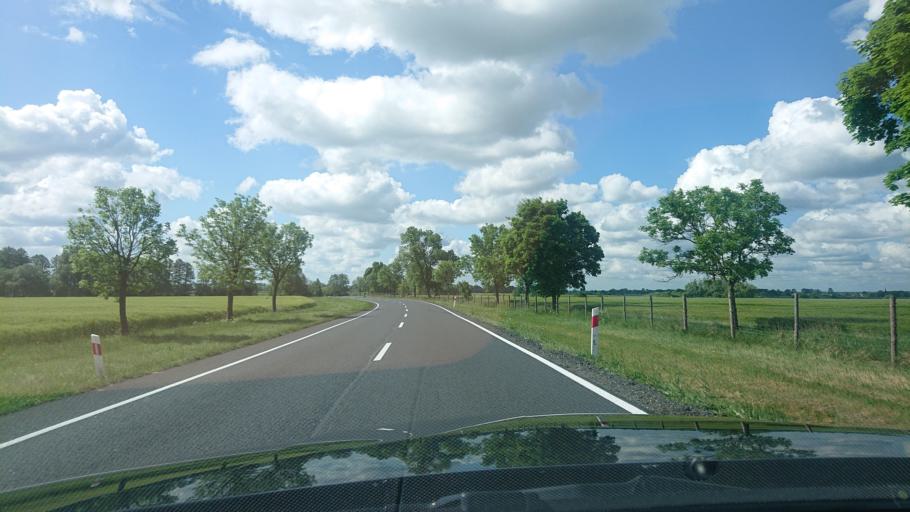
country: PL
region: Lower Silesian Voivodeship
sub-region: Powiat polkowicki
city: Radwanice
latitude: 51.5604
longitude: 15.9347
